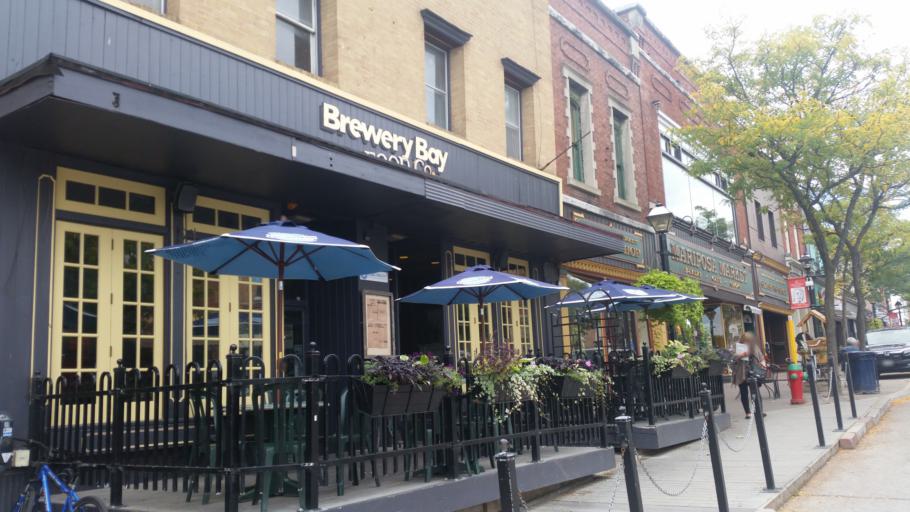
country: CA
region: Ontario
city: Orillia
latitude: 44.6095
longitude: -79.4166
